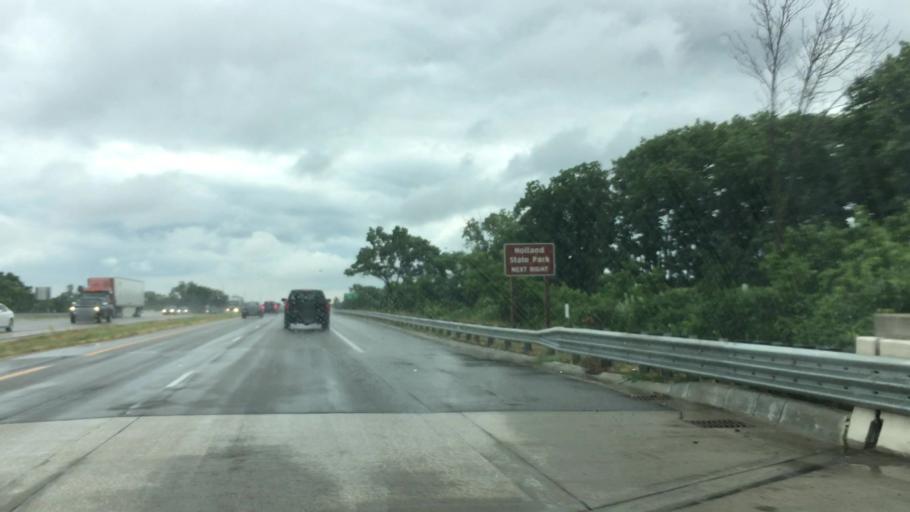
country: US
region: Michigan
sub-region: Ottawa County
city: Holland
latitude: 42.8014
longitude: -86.0835
